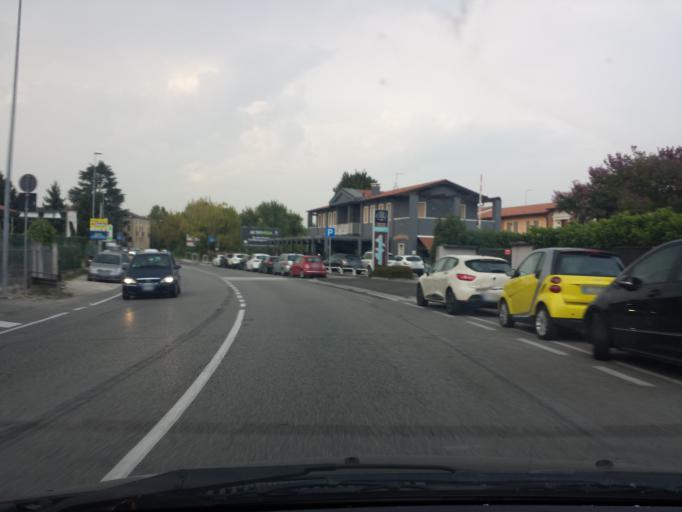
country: IT
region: Veneto
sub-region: Provincia di Vicenza
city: Monticello Conte Otto
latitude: 45.5778
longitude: 11.5524
